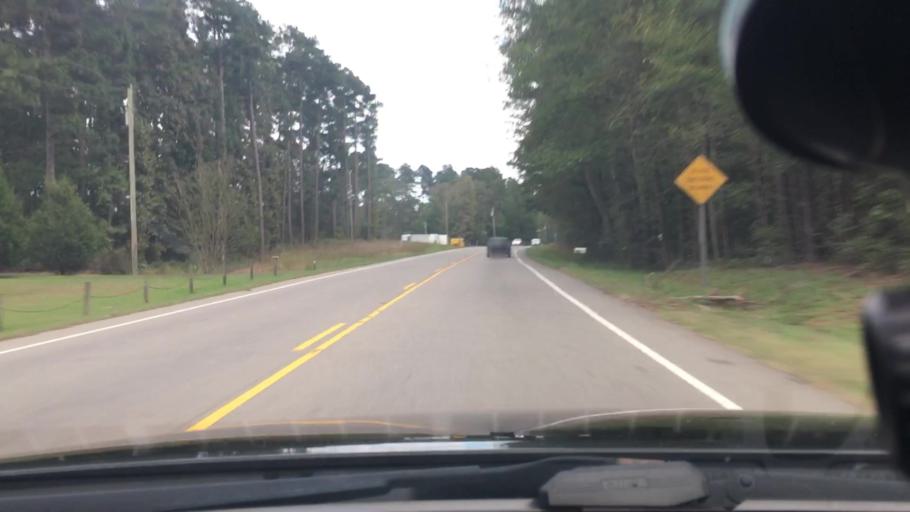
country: US
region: North Carolina
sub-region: Moore County
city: Carthage
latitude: 35.3804
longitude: -79.4780
